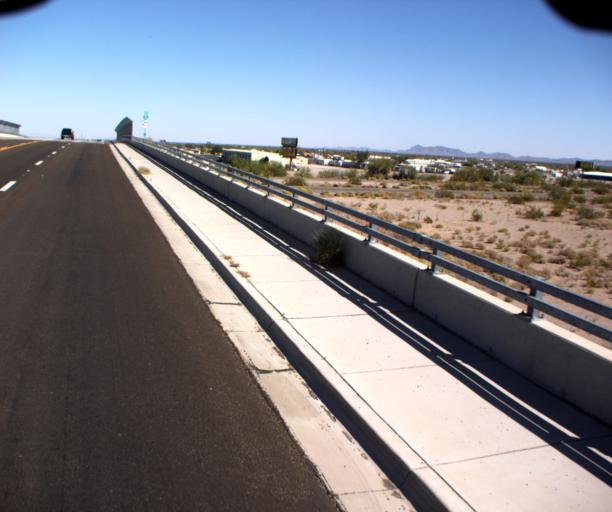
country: US
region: Arizona
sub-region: La Paz County
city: Quartzsite
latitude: 33.6620
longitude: -114.2170
